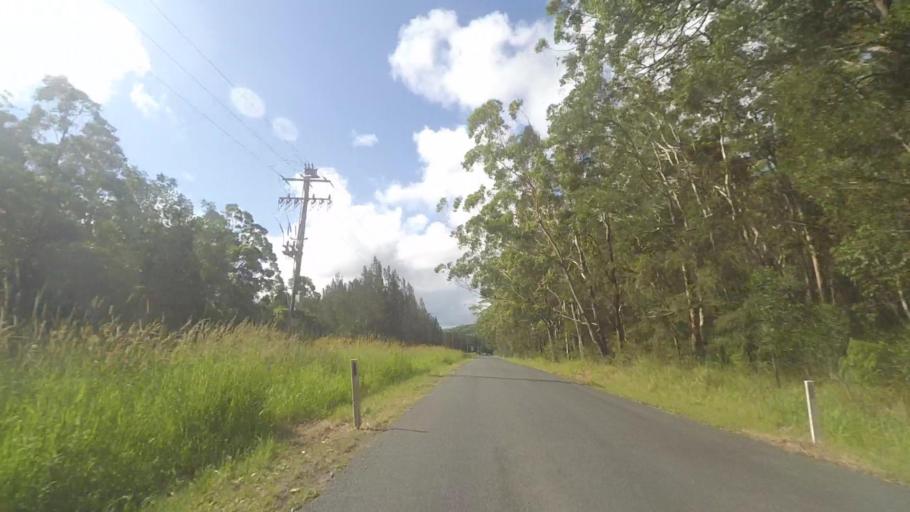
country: AU
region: New South Wales
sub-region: Great Lakes
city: Forster
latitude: -32.4035
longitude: 152.4614
